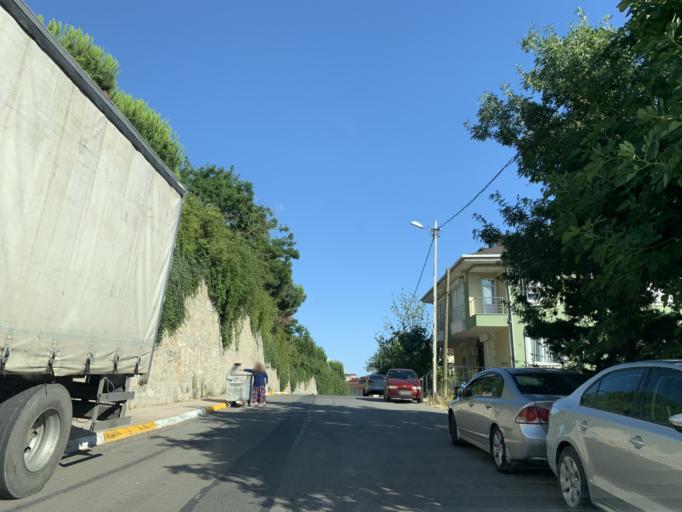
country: TR
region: Istanbul
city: Pendik
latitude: 40.8900
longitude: 29.2508
